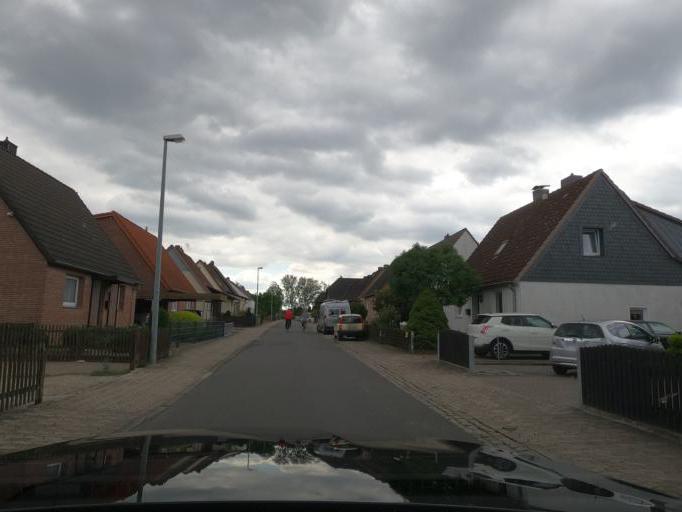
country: DE
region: Lower Saxony
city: Lehrte
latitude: 52.3753
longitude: 9.9099
